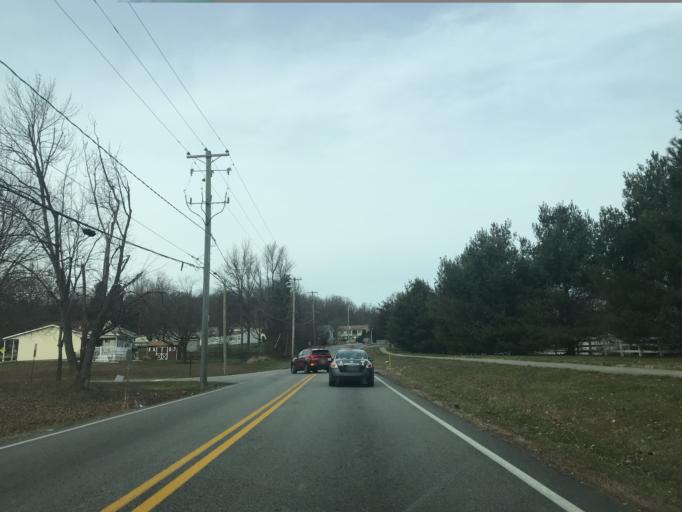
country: US
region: Maryland
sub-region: Cecil County
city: Elkton
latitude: 39.6095
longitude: -75.7913
